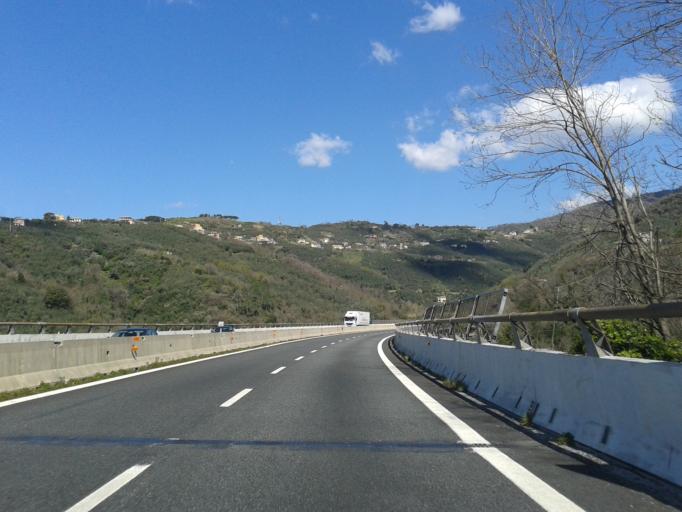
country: IT
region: Liguria
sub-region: Provincia di Genova
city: Sestri Levante
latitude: 44.2946
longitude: 9.3842
